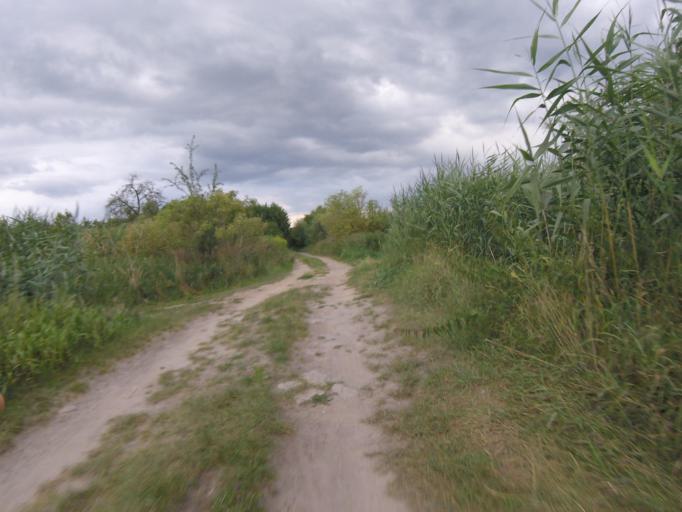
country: DE
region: Brandenburg
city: Mittenwalde
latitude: 52.2730
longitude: 13.5273
